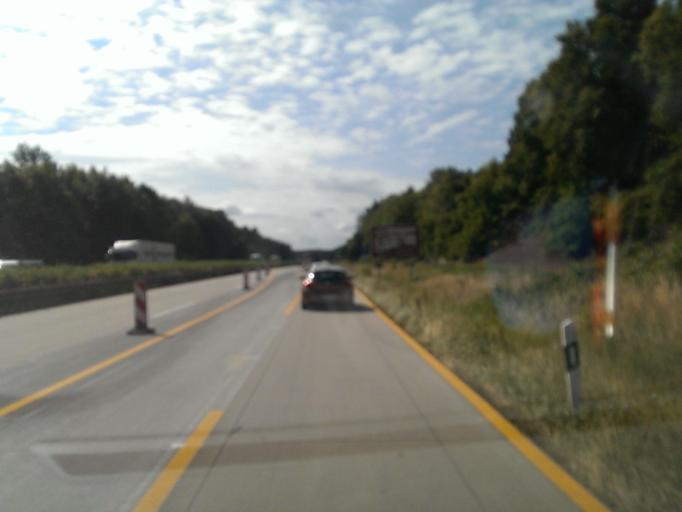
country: DE
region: Brandenburg
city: Schwerin
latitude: 52.1845
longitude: 13.6184
